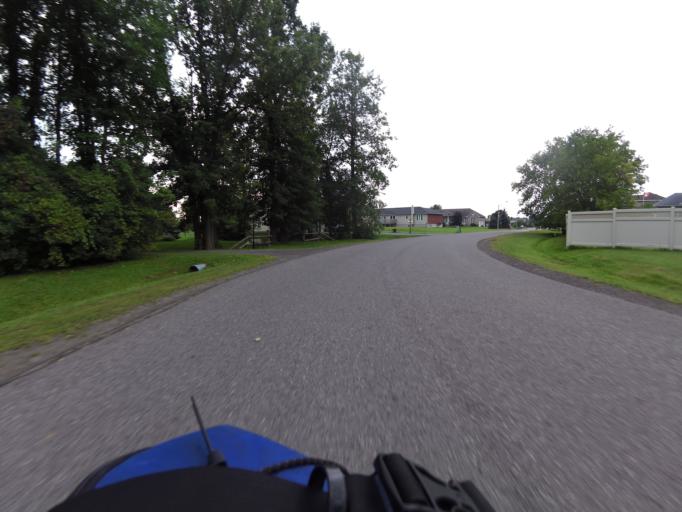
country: CA
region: Ontario
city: Ottawa
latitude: 45.2283
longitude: -75.4762
